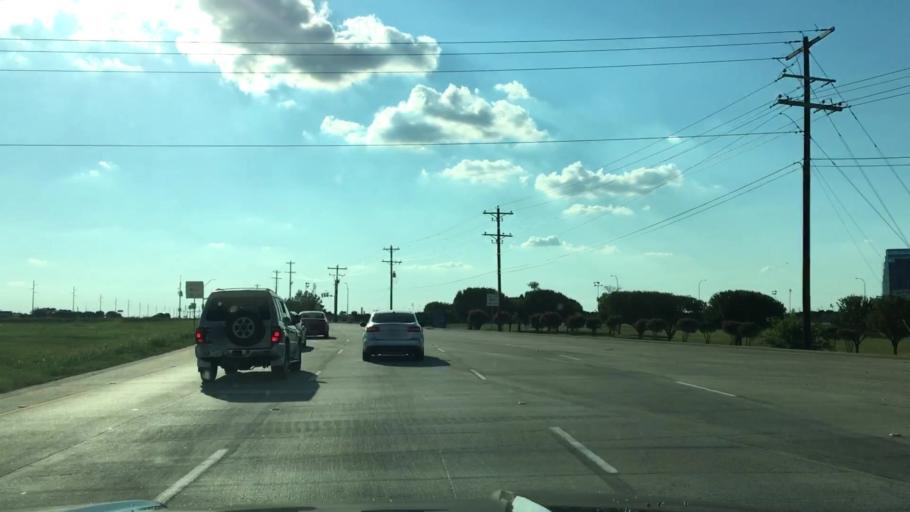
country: US
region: Texas
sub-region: Denton County
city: Roanoke
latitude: 33.0270
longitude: -97.2760
